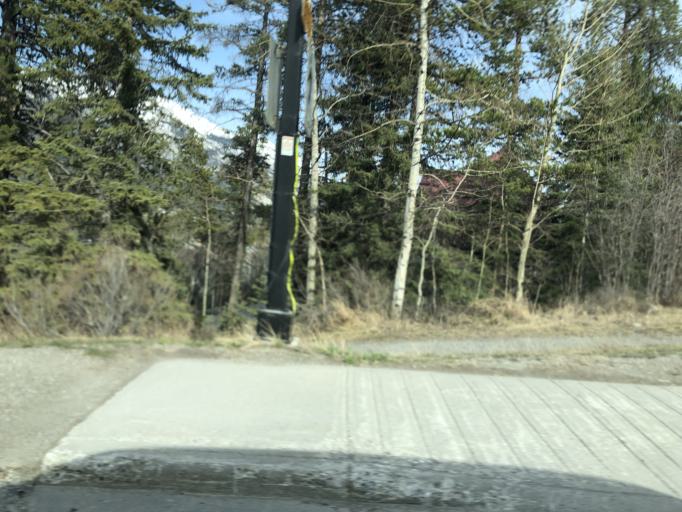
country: CA
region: Alberta
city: Canmore
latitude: 51.0773
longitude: -115.3652
